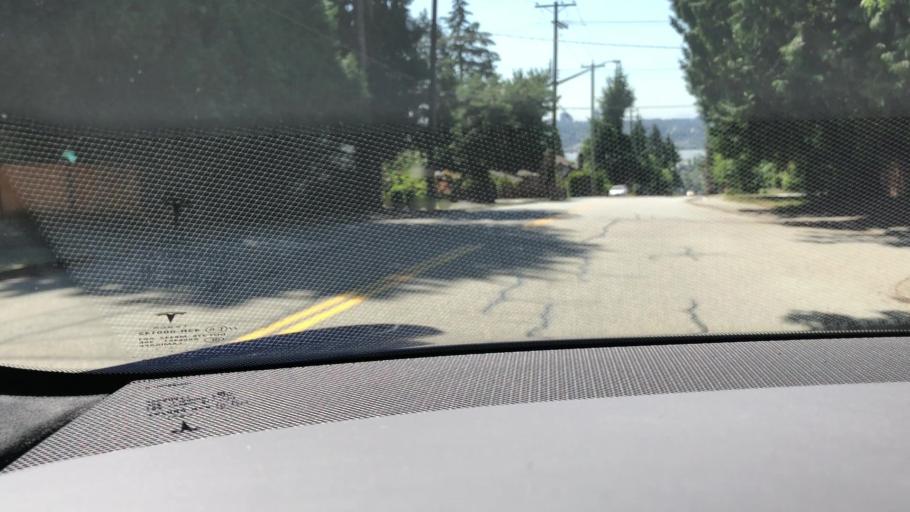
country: CA
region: British Columbia
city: Port Moody
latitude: 49.2478
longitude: -122.8653
